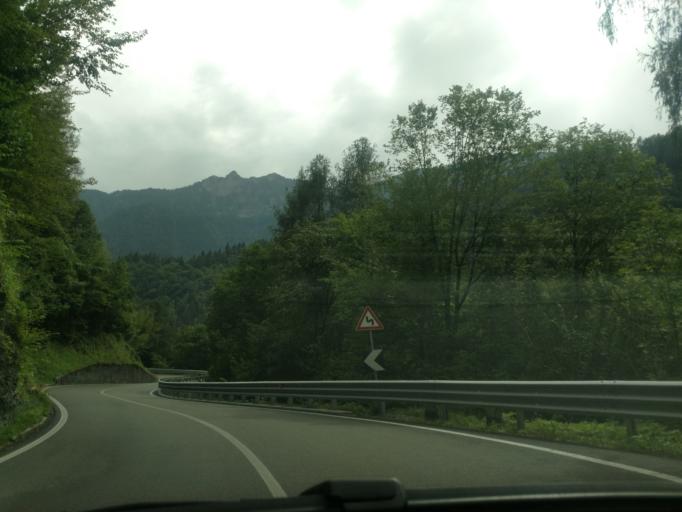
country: IT
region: Veneto
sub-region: Provincia di Belluno
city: Longarone
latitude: 46.2727
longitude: 12.2524
